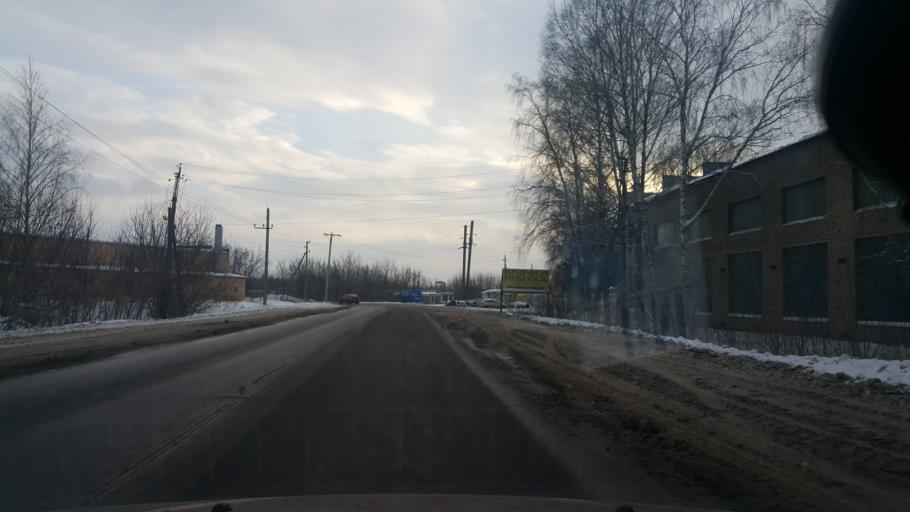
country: RU
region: Tambov
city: Pokrovo-Prigorodnoye
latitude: 52.6562
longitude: 41.4226
